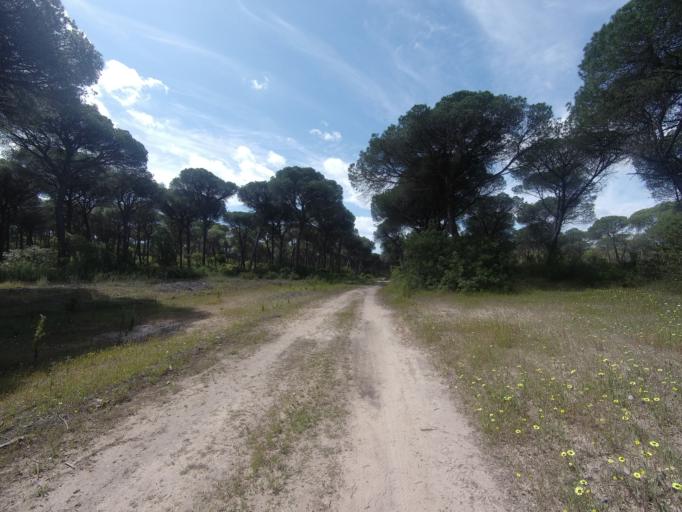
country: ES
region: Andalusia
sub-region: Provincia de Huelva
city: Aljaraque
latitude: 37.2281
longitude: -7.0670
